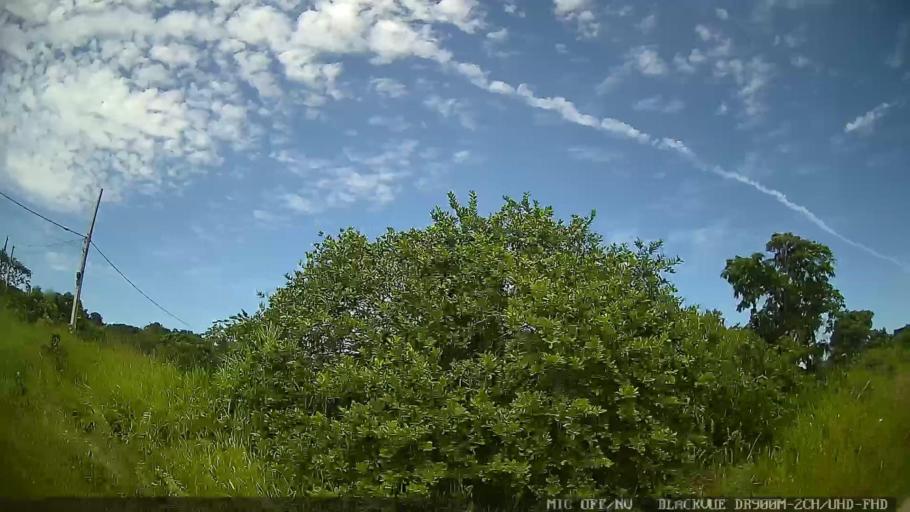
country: BR
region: Sao Paulo
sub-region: Iguape
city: Iguape
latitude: -24.7187
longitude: -47.5245
